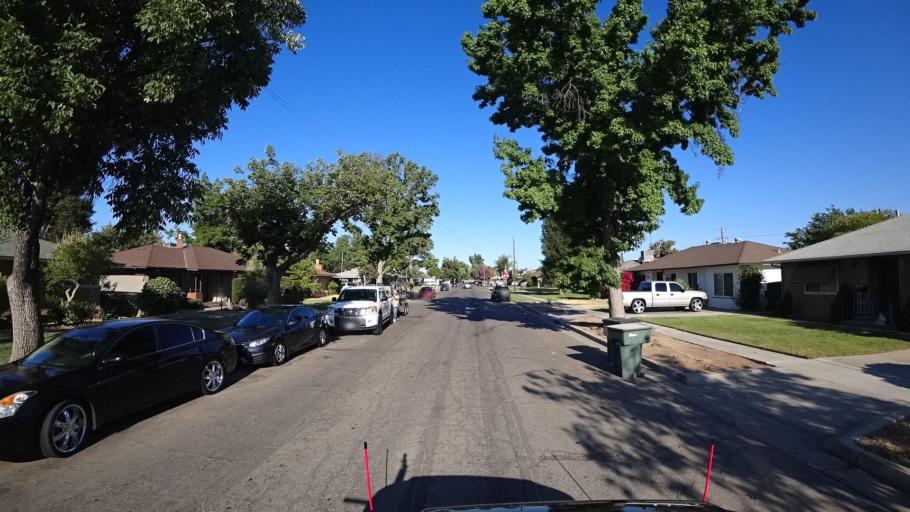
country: US
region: California
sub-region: Fresno County
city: Fresno
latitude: 36.7683
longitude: -119.8282
